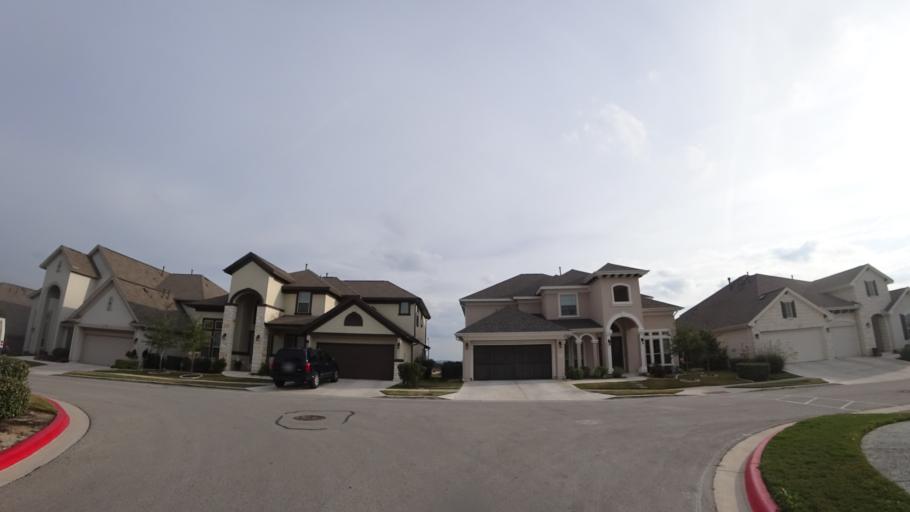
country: US
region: Texas
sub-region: Travis County
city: Hudson Bend
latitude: 30.3784
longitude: -97.8801
